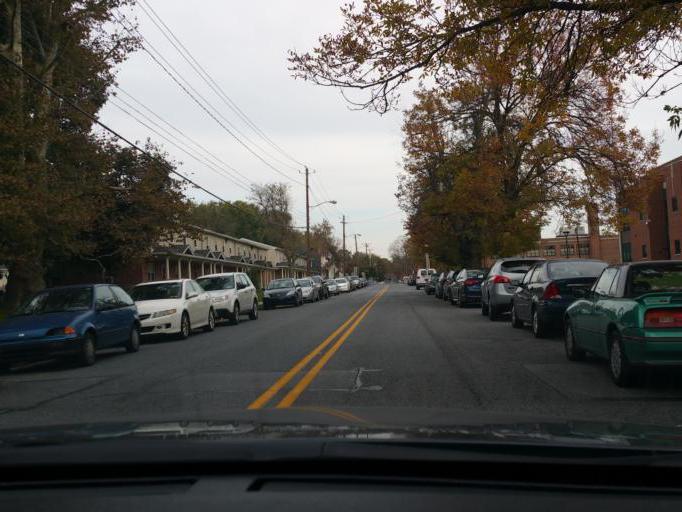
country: US
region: Pennsylvania
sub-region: Lancaster County
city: Lancaster
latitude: 40.0304
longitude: -76.2931
